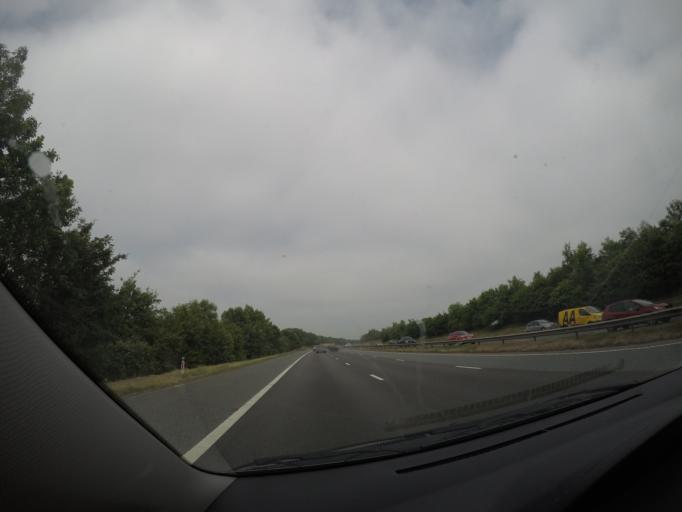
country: GB
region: England
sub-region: North Yorkshire
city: Boroughbridge
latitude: 54.1040
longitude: -1.4145
